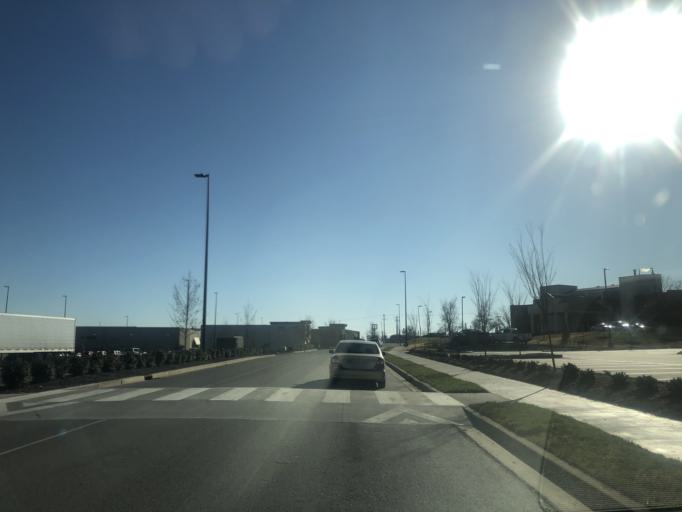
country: US
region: Tennessee
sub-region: Davidson County
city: Belle Meade
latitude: 36.0812
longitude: -86.9511
